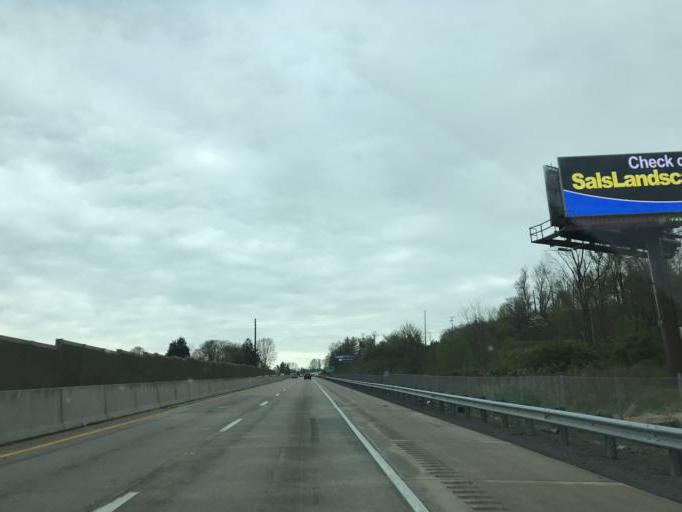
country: US
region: Pennsylvania
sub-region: Lancaster County
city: Adamstown
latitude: 40.2591
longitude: -76.0339
